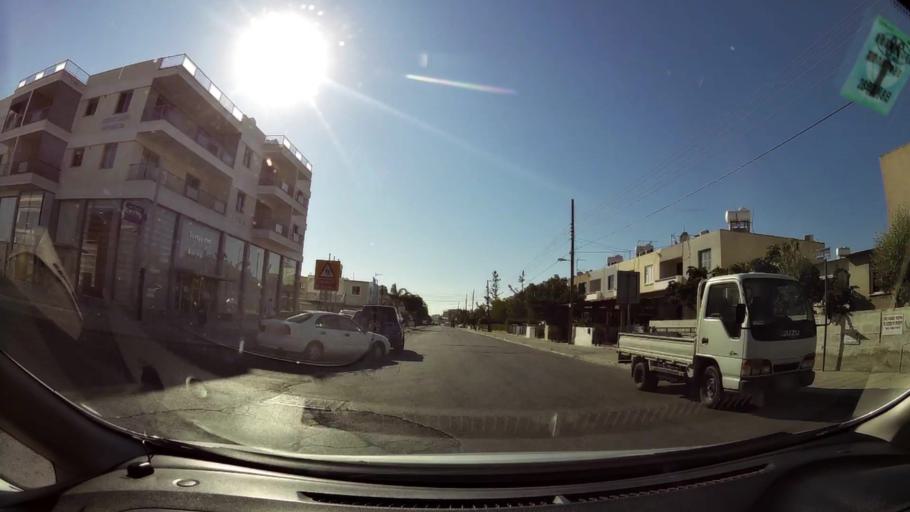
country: CY
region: Larnaka
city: Larnaca
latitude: 34.9361
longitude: 33.6125
